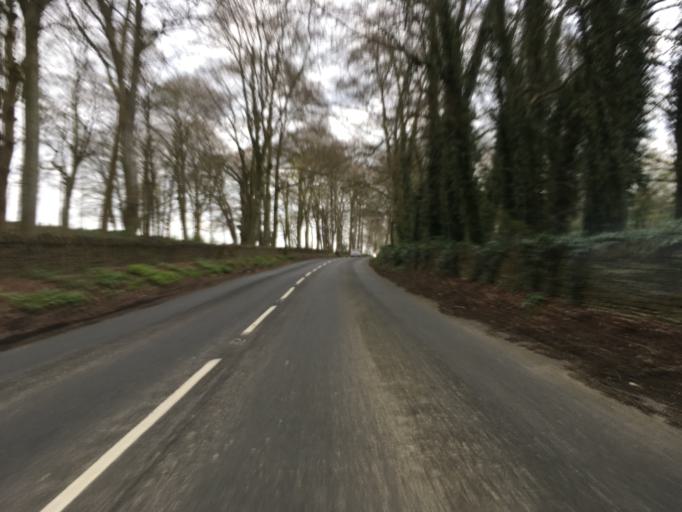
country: GB
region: England
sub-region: Gloucestershire
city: Northleach
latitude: 51.7612
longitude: -1.8281
